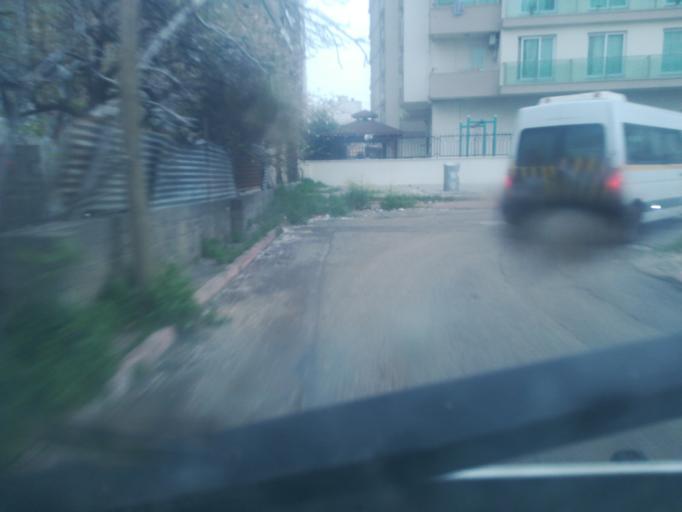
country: TR
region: Adana
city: Seyhan
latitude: 37.0107
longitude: 35.3036
